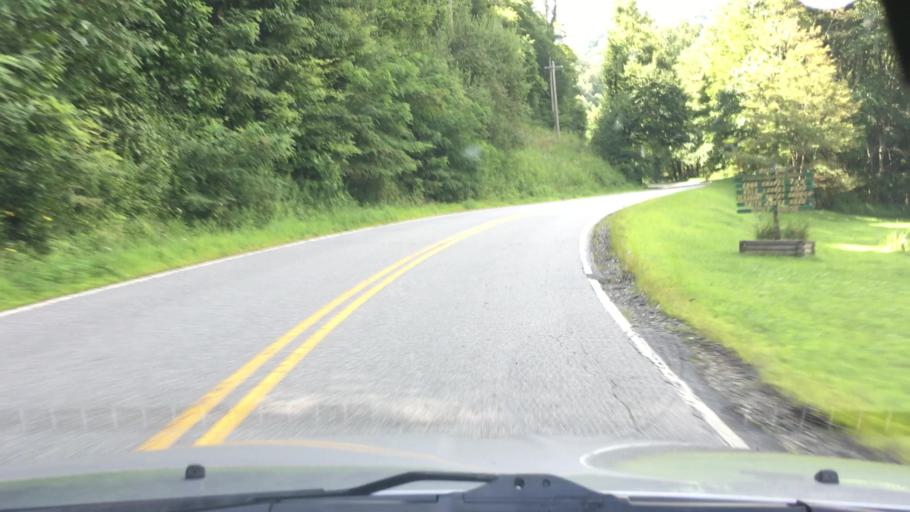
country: US
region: North Carolina
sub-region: Madison County
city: Mars Hill
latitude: 35.9100
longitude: -82.5451
